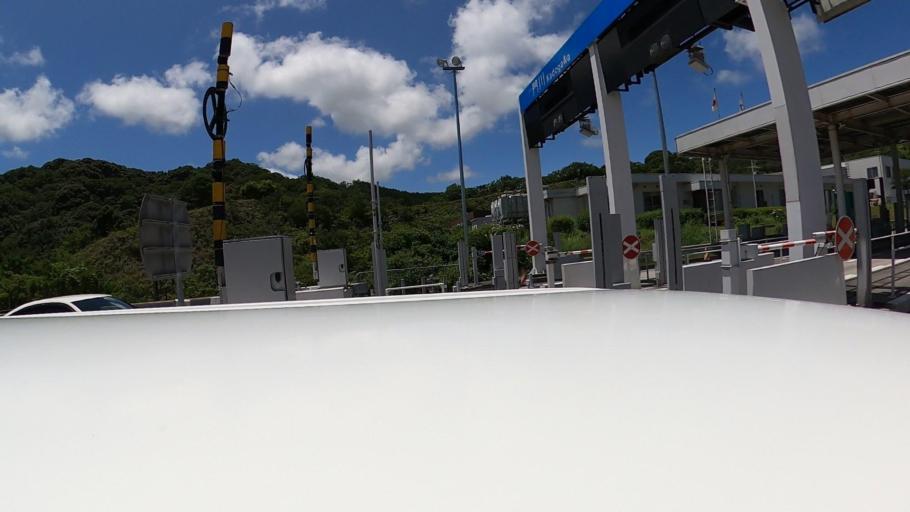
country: JP
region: Miyazaki
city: Nobeoka
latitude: 32.5028
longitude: 131.6619
